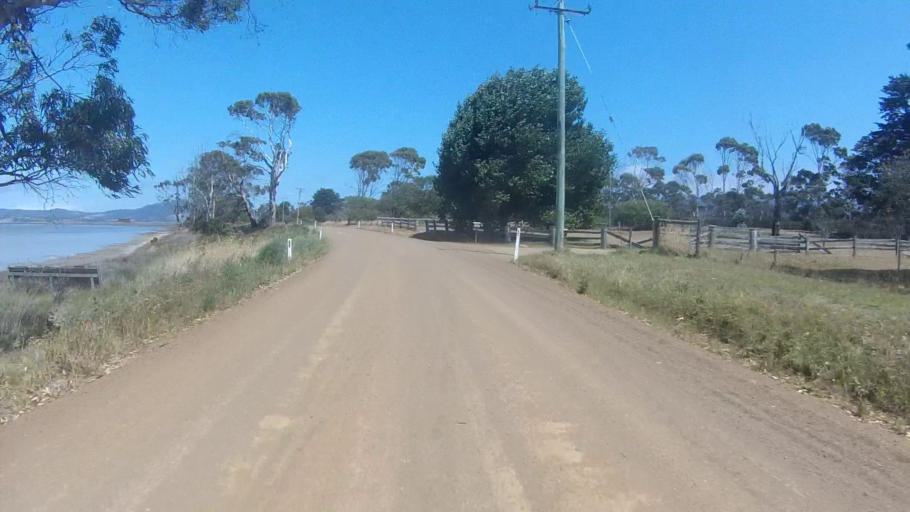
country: AU
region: Tasmania
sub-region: Sorell
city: Sorell
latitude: -42.8377
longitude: 147.8533
